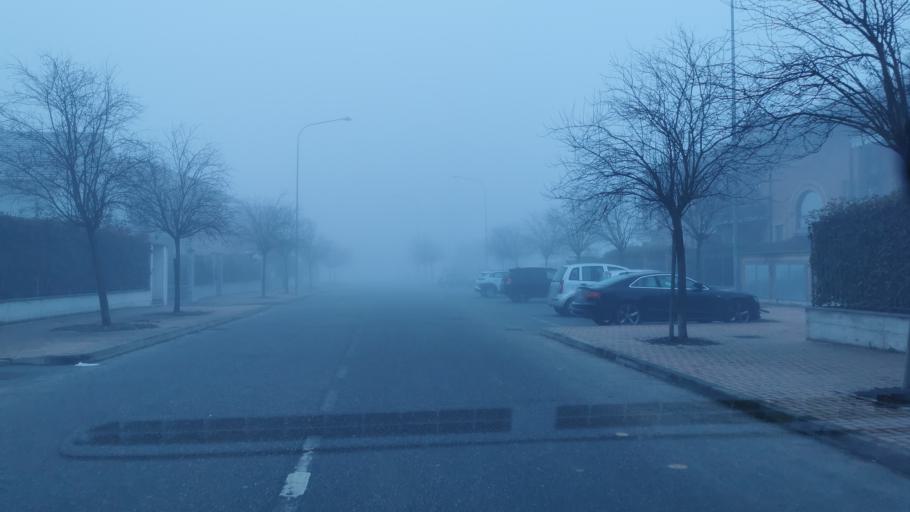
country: IT
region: Piedmont
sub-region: Provincia di Torino
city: Volpiano
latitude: 45.1931
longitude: 7.7663
